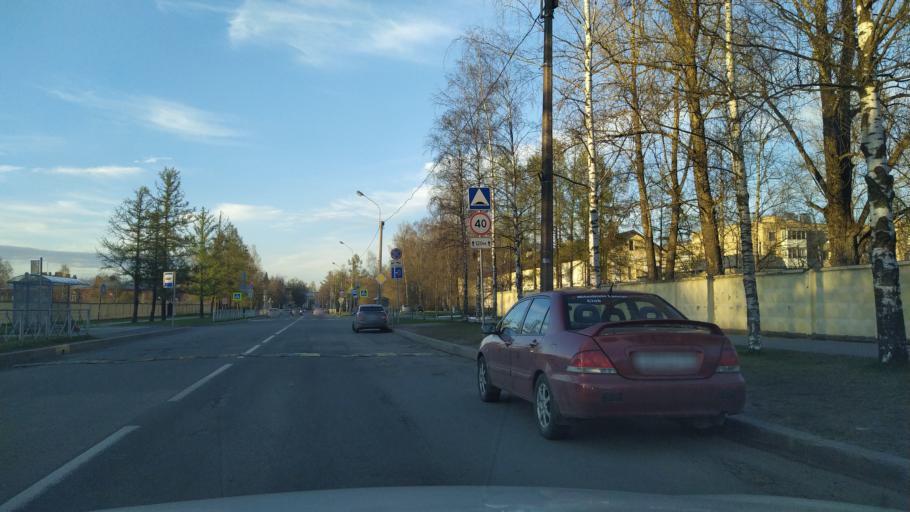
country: RU
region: St.-Petersburg
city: Pushkin
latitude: 59.7058
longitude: 30.3761
